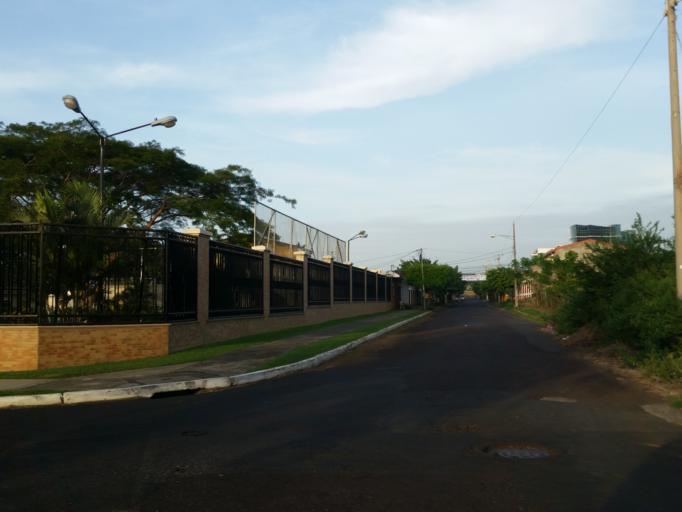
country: NI
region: Managua
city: Managua
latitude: 12.1145
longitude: -86.2709
